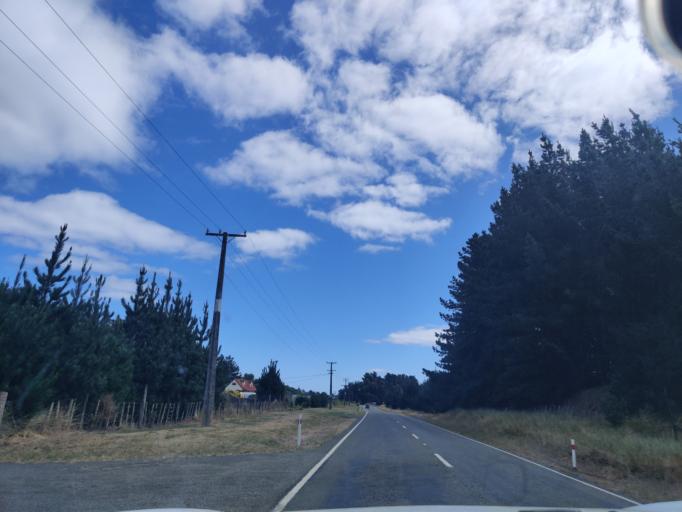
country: NZ
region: Manawatu-Wanganui
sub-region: Horowhenua District
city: Foxton
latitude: -40.3756
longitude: 175.2513
